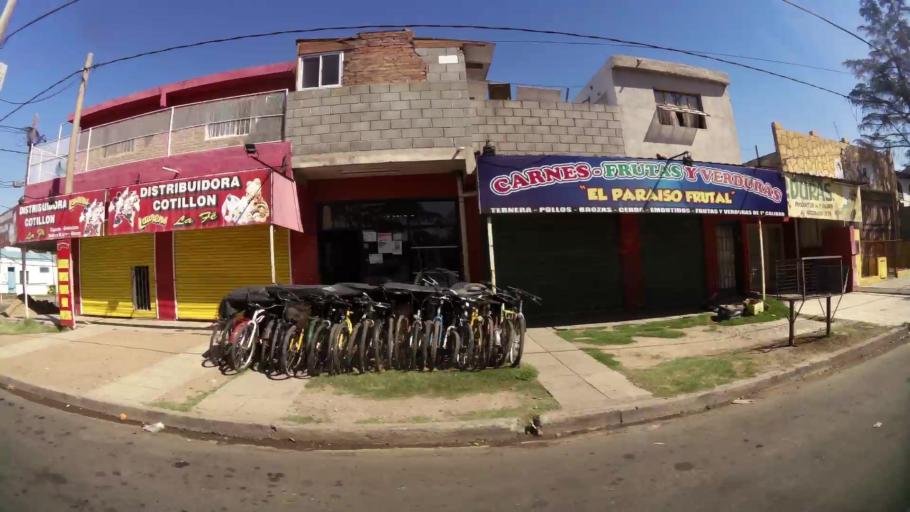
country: AR
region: Cordoba
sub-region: Departamento de Capital
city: Cordoba
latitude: -31.3721
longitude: -64.1696
